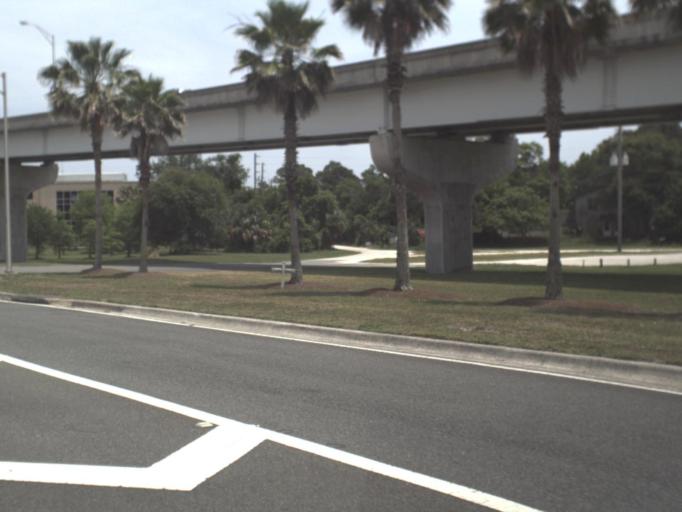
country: US
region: Florida
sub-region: Duval County
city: Atlantic Beach
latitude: 30.3243
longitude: -81.4223
